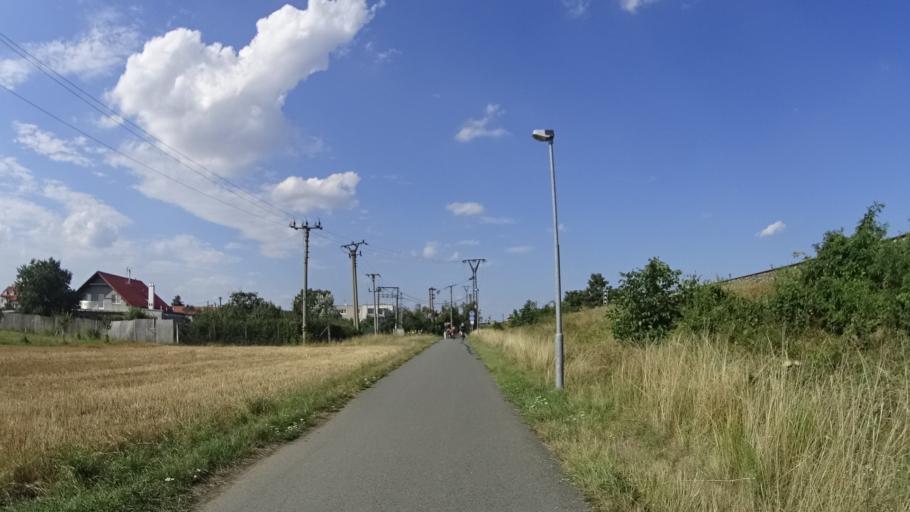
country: CZ
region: Zlin
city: Kunovice
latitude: 49.0448
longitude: 17.4620
